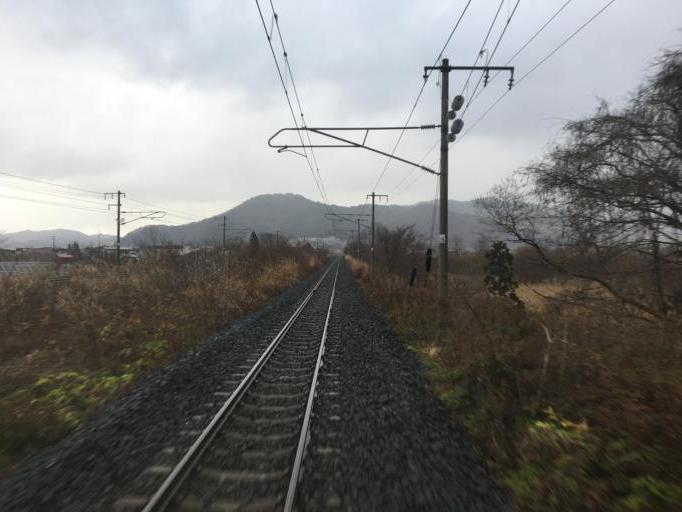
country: JP
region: Aomori
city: Aomori Shi
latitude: 40.8687
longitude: 140.8404
